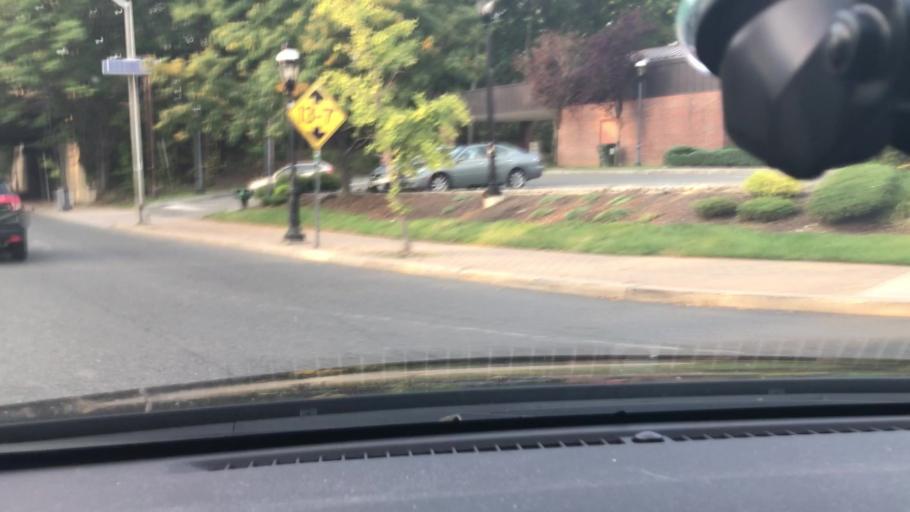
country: US
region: New Jersey
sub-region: Union County
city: Cranford
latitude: 40.6553
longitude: -74.3000
